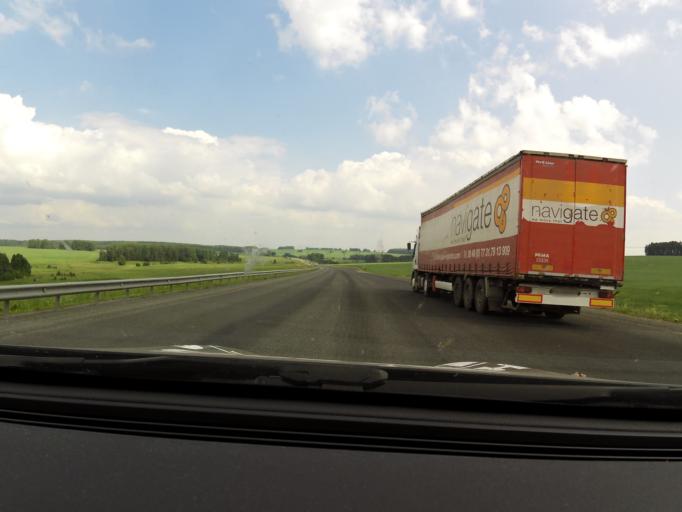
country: RU
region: Sverdlovsk
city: Ufimskiy
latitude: 56.7749
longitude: 57.9988
